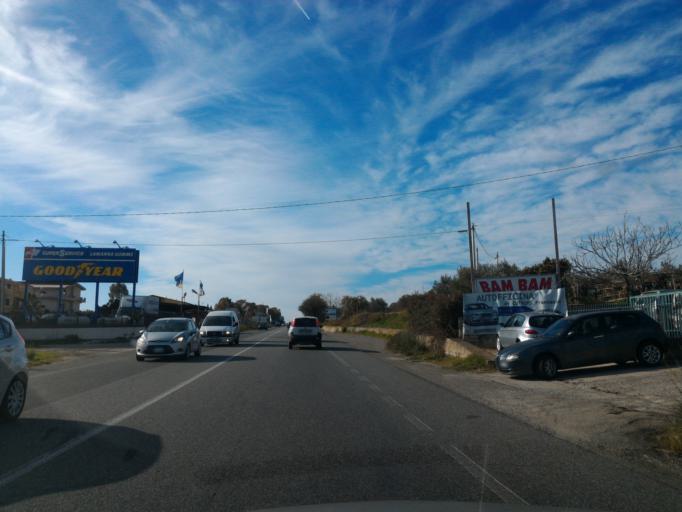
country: IT
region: Calabria
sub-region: Provincia di Catanzaro
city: Sellia Marina
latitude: 38.8917
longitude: 16.7211
